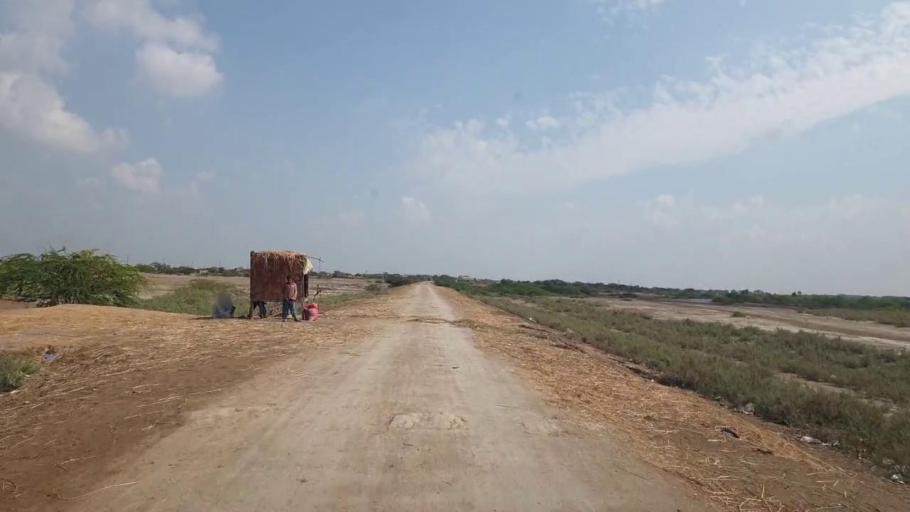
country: PK
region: Sindh
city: Badin
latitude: 24.4781
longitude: 68.6046
